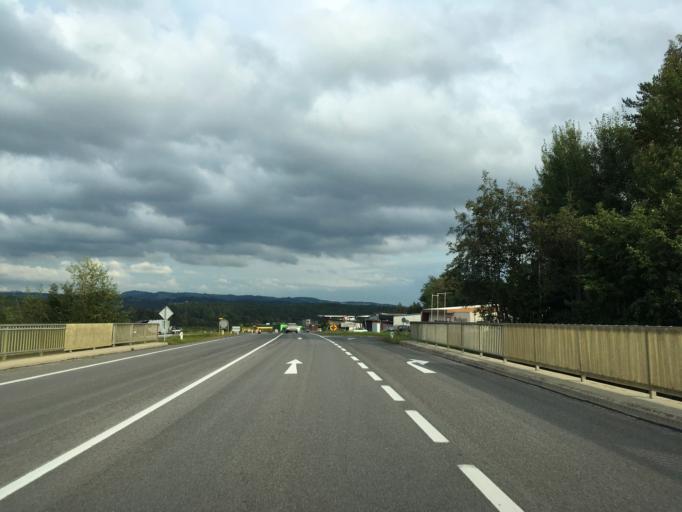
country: AT
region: Styria
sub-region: Politischer Bezirk Hartberg-Fuerstenfeld
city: Dechantskirchen
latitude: 47.4145
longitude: 16.0196
